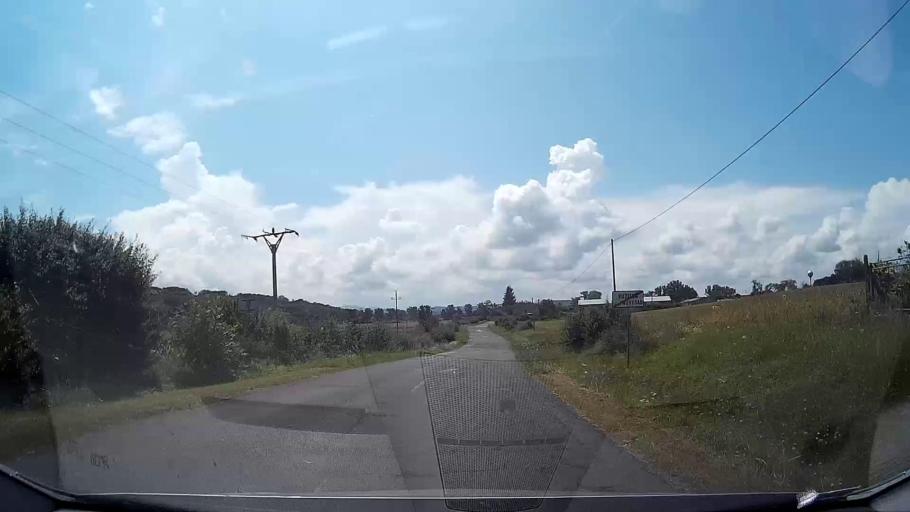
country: SK
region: Banskobystricky
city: Fil'akovo
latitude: 48.3251
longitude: 19.8165
